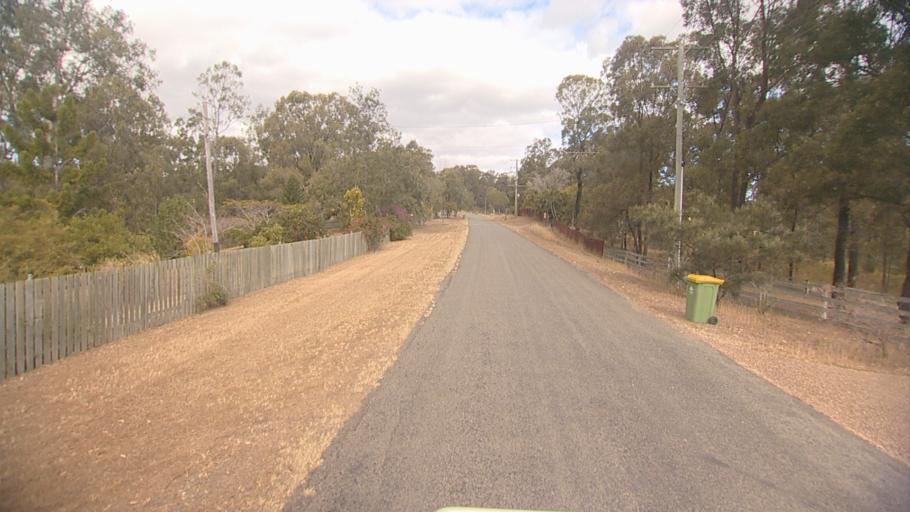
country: AU
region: Queensland
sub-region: Logan
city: Cedar Vale
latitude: -27.8889
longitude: 153.0235
